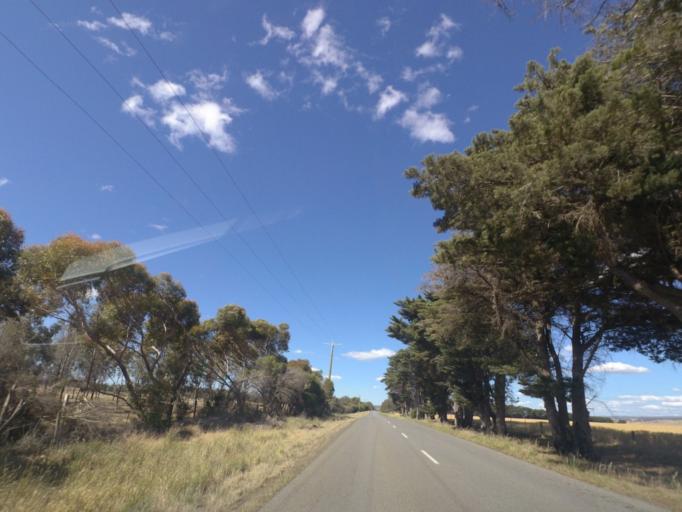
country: AU
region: Victoria
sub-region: Hume
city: Craigieburn
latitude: -37.4200
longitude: 144.8771
